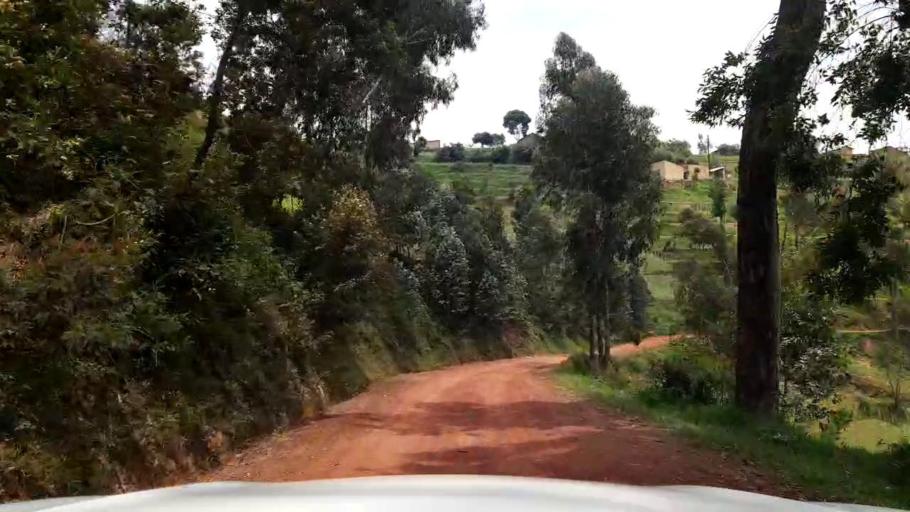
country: RW
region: Northern Province
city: Byumba
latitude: -1.5096
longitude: 29.9388
